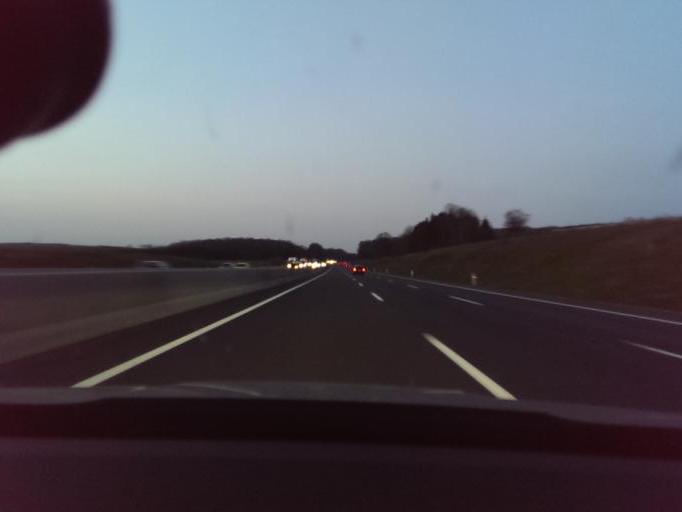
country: DE
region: Lower Saxony
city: Bockenem
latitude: 52.0252
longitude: 10.1706
